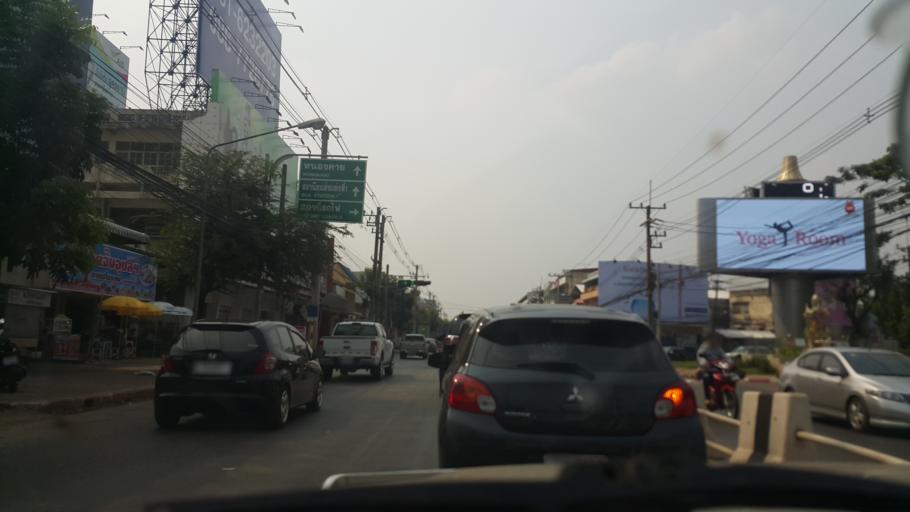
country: TH
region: Changwat Udon Thani
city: Udon Thani
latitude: 17.3985
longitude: 102.8047
